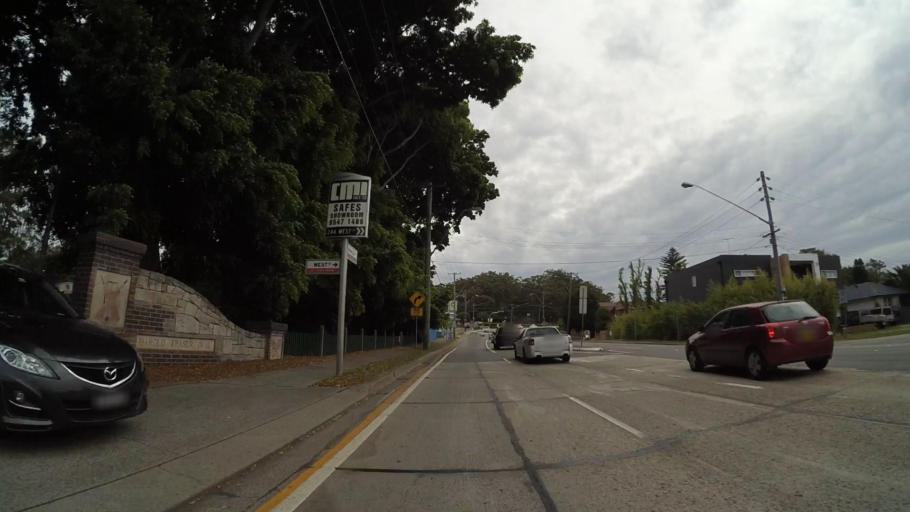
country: AU
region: New South Wales
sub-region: Kogarah
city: Kogarah
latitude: -33.9813
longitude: 151.1186
